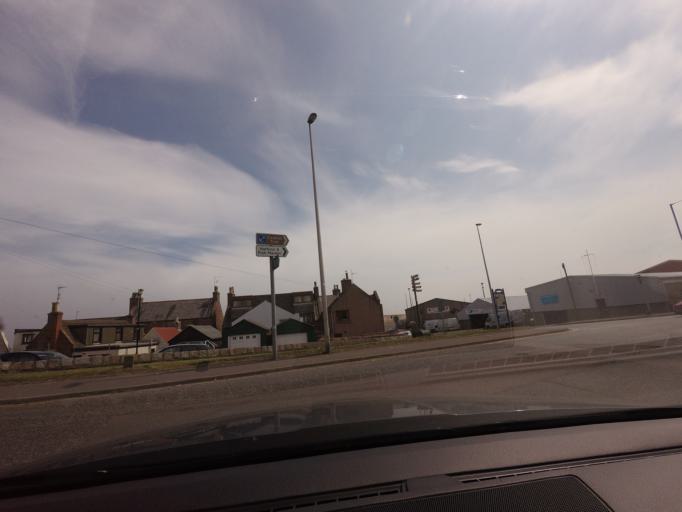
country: GB
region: Scotland
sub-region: Aberdeenshire
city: Peterhead
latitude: 57.5092
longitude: -1.7753
